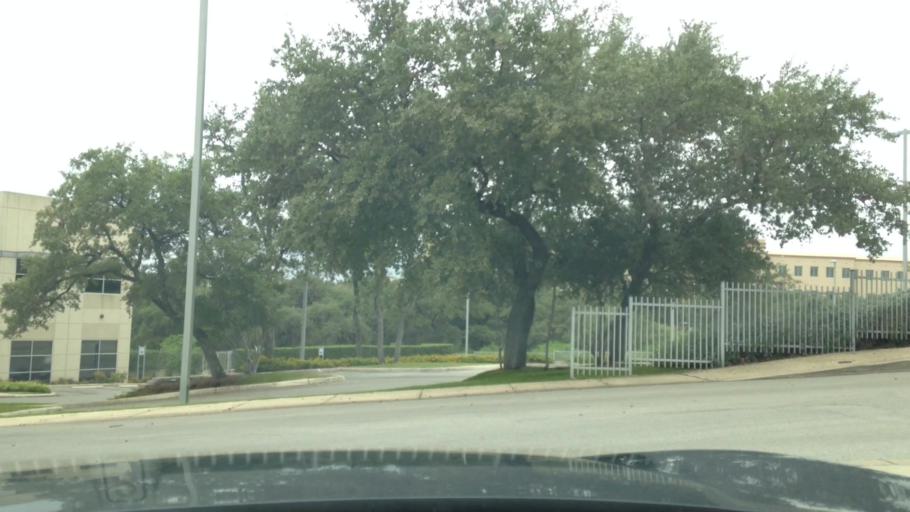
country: US
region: Texas
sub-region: Bexar County
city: Hollywood Park
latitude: 29.6163
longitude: -98.4820
